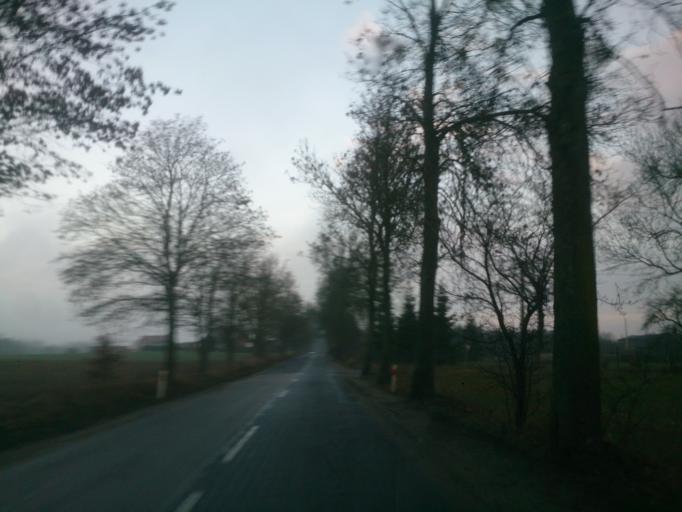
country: PL
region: Pomeranian Voivodeship
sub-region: Powiat starogardzki
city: Skorcz
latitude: 53.8192
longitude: 18.4652
